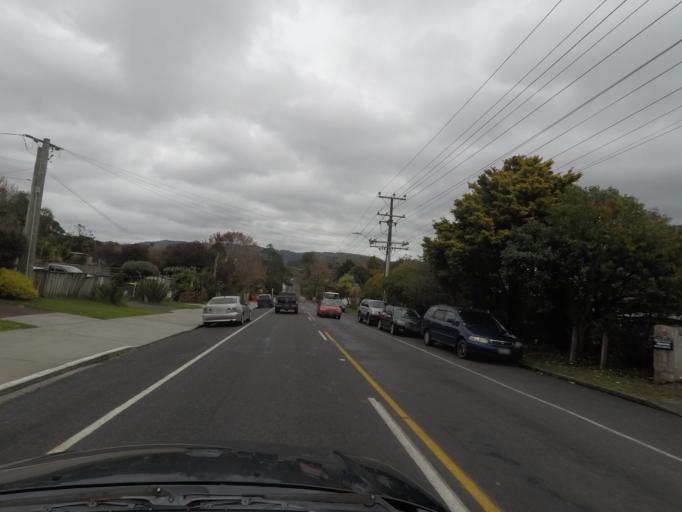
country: NZ
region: Auckland
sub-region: Auckland
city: Waitakere
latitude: -36.9093
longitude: 174.6252
